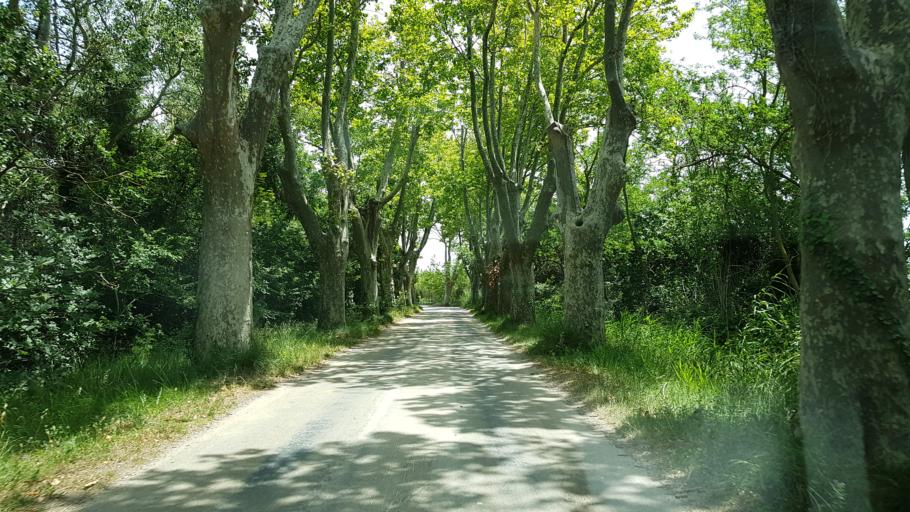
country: FR
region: Provence-Alpes-Cote d'Azur
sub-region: Departement des Bouches-du-Rhone
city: Port-Saint-Louis-du-Rhone
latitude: 43.4485
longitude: 4.6611
